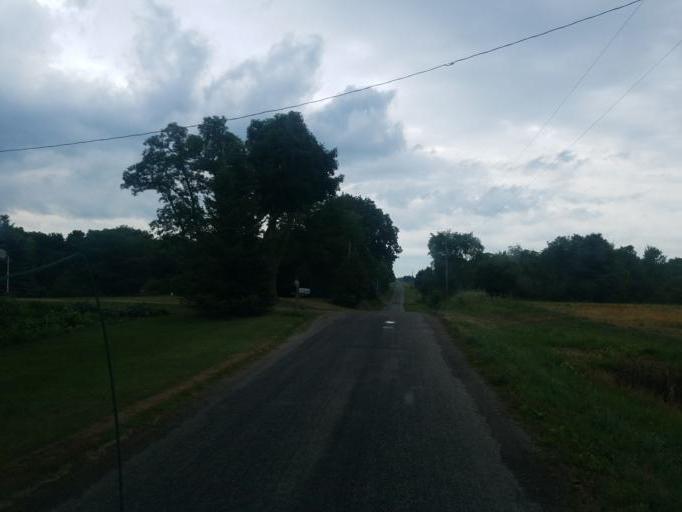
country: US
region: Ohio
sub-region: Defiance County
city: Hicksville
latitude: 41.3681
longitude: -84.7982
